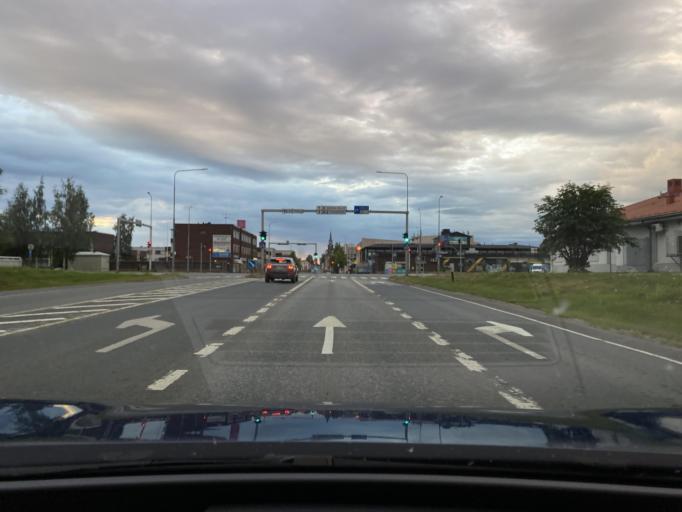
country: FI
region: Northern Ostrobothnia
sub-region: Raahe
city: Raahe
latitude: 64.6826
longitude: 24.4797
